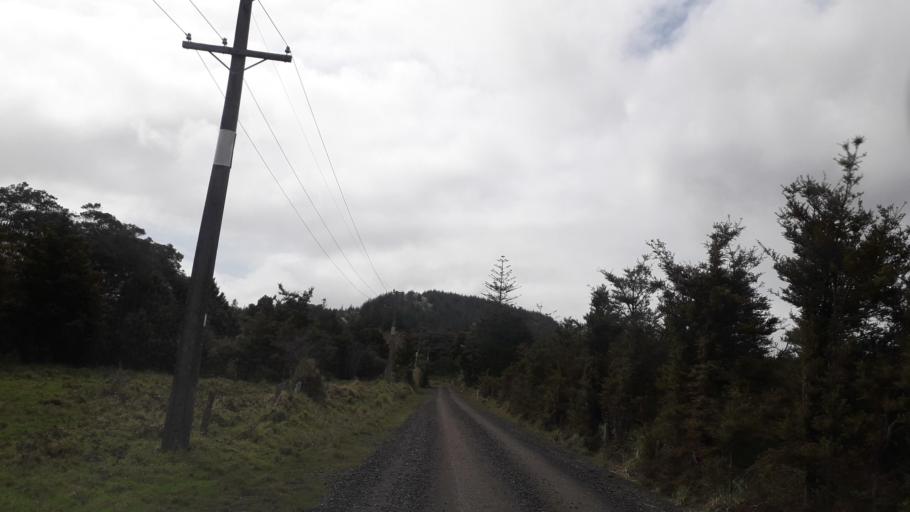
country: NZ
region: Northland
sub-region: Far North District
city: Kaitaia
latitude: -35.3782
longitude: 173.4109
